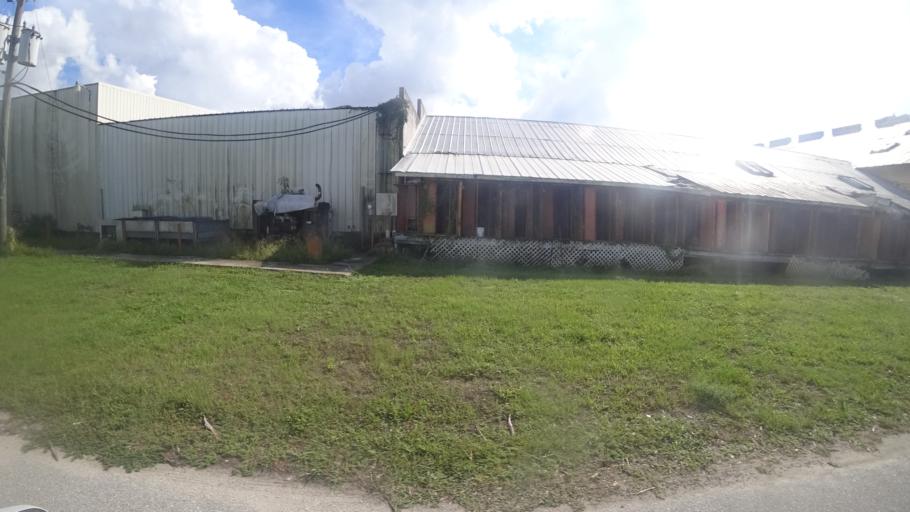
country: US
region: Florida
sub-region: Manatee County
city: Memphis
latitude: 27.5432
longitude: -82.5805
